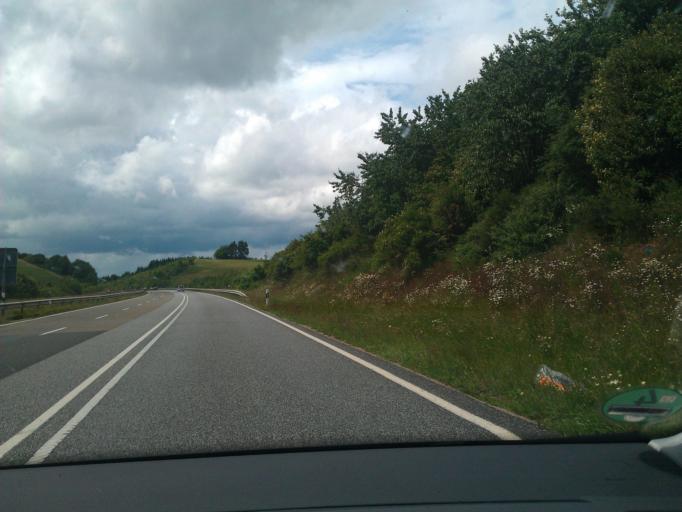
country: DE
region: Rheinland-Pfalz
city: Grosslangenfeld
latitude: 50.2157
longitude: 6.2361
